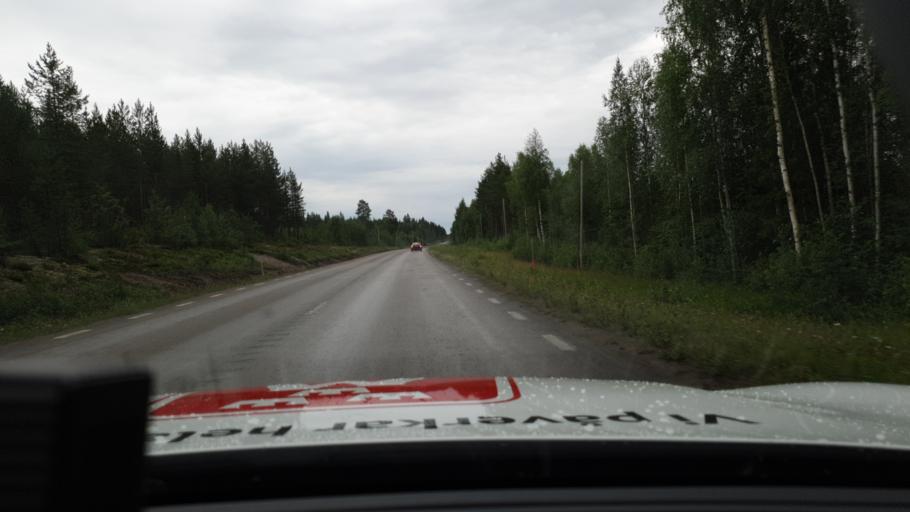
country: SE
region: Norrbotten
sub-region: Alvsbyns Kommun
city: AElvsbyn
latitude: 66.1216
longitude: 20.9210
